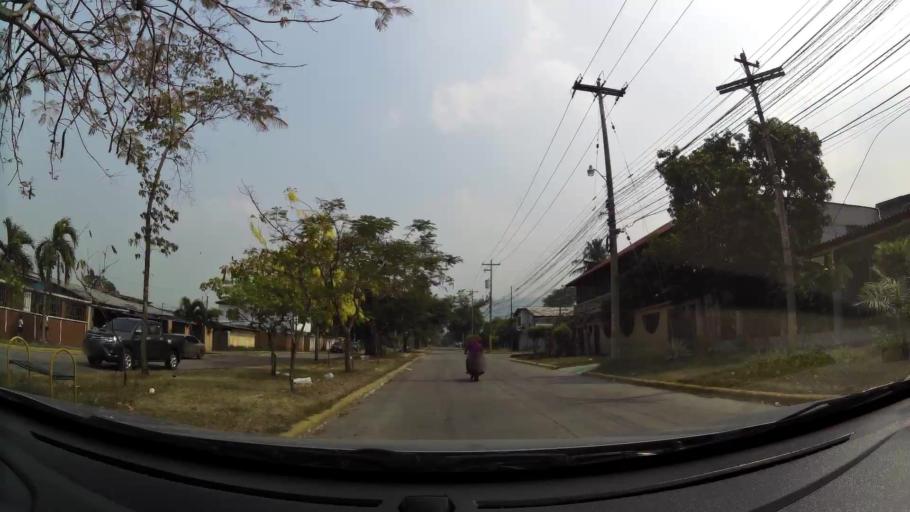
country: HN
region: Cortes
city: San Pedro Sula
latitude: 15.4874
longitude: -88.0329
